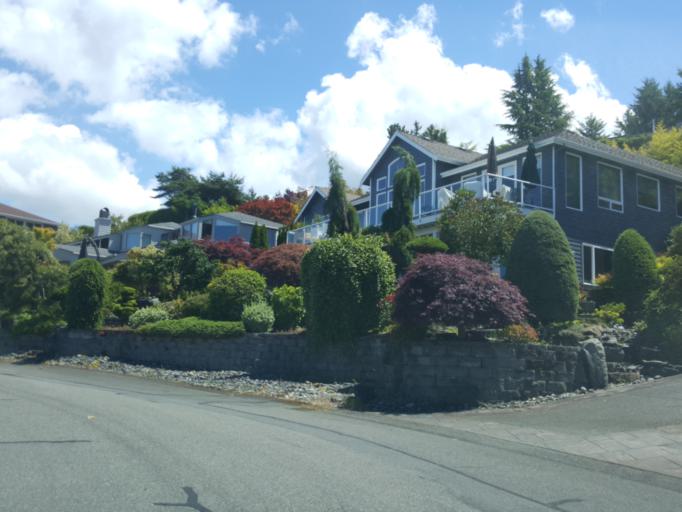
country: US
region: Washington
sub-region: Pierce County
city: University Place
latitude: 47.2140
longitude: -122.5743
